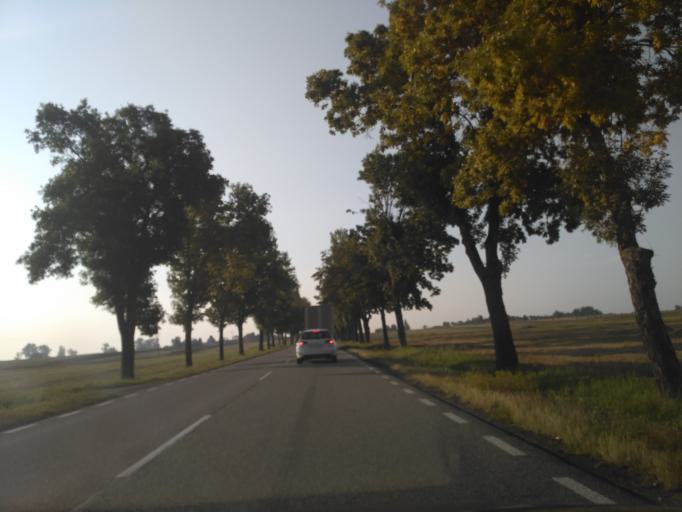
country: PL
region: Lublin Voivodeship
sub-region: Powiat krasnicki
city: Szastarka
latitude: 50.8394
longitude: 22.2997
